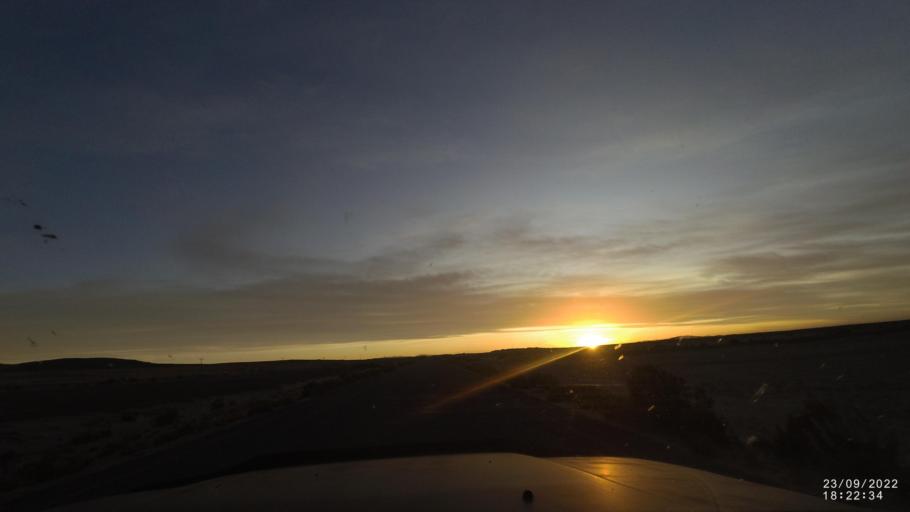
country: BO
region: Oruro
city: Challapata
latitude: -19.2894
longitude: -67.0884
